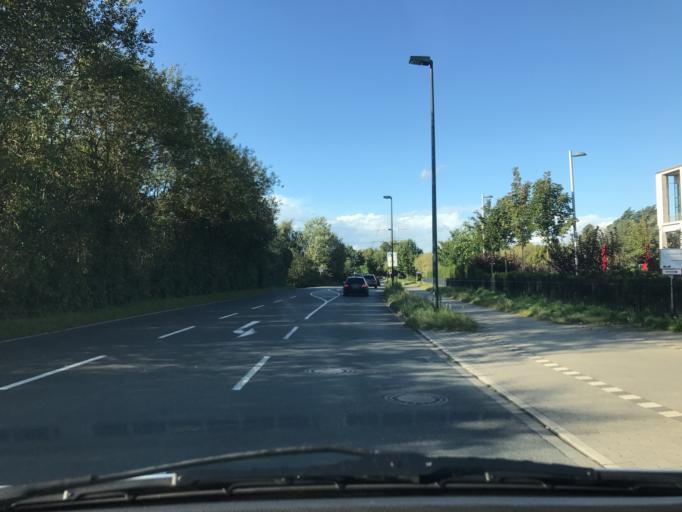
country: DE
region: North Rhine-Westphalia
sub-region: Regierungsbezirk Dusseldorf
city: Ratingen
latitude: 51.2776
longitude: 6.8064
